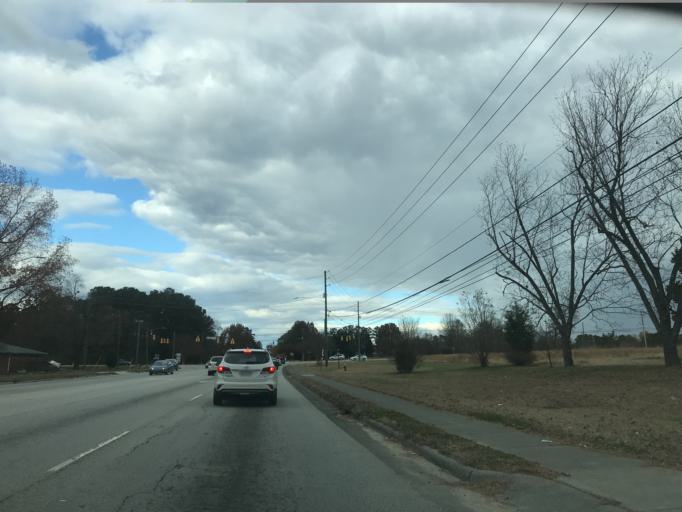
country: US
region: North Carolina
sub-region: Wake County
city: Raleigh
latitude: 35.8299
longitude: -78.5692
